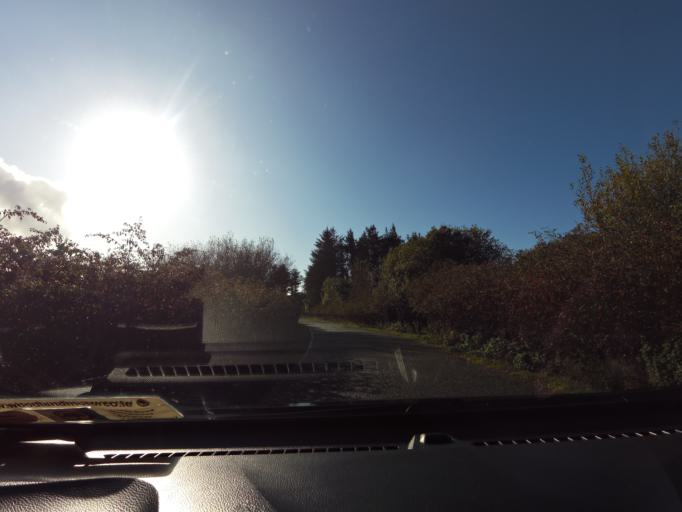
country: IE
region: Connaught
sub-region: Maigh Eo
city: Westport
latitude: 53.8846
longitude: -9.8109
